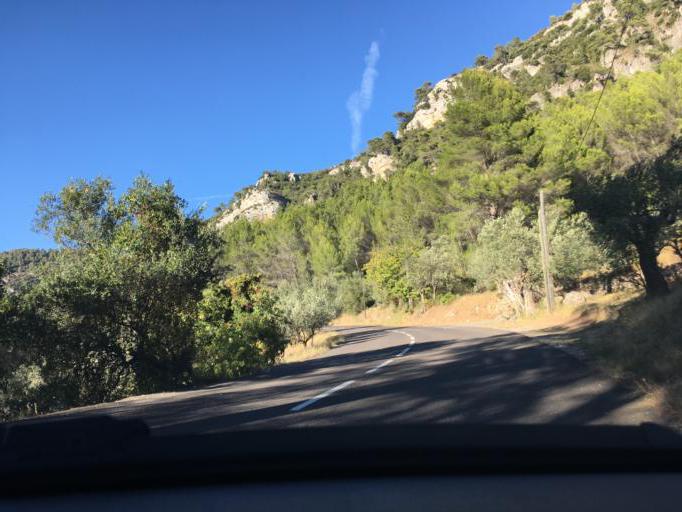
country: FR
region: Provence-Alpes-Cote d'Azur
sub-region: Departement du Var
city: Flayosc
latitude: 43.5789
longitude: 6.4250
